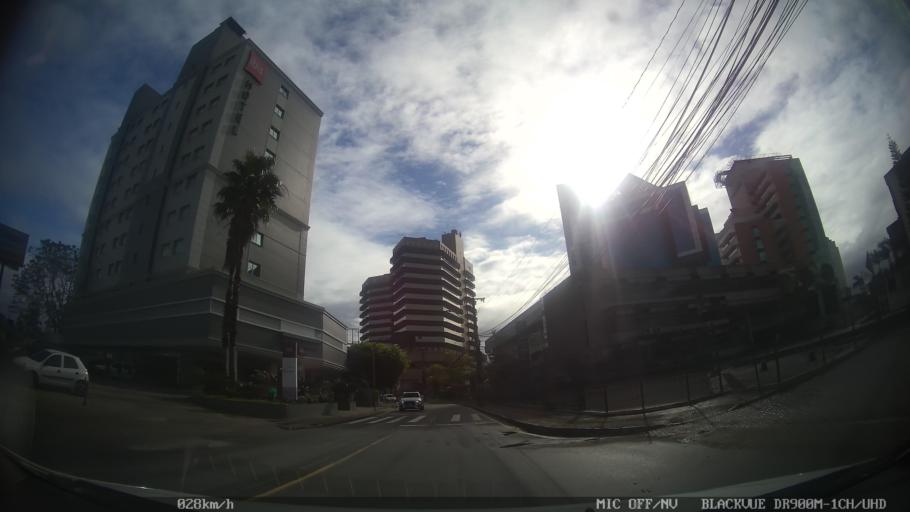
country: BR
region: Santa Catarina
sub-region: Sao Jose
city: Campinas
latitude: -27.5875
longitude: -48.6126
